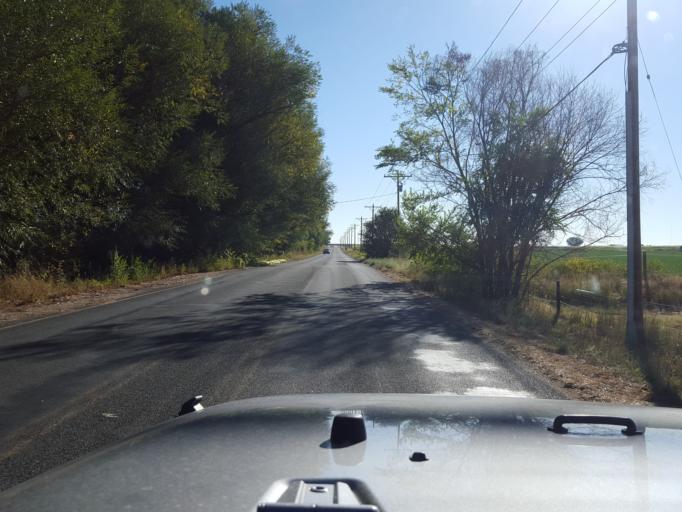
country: US
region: Colorado
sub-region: Weld County
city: Firestone
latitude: 40.1315
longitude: -104.9929
